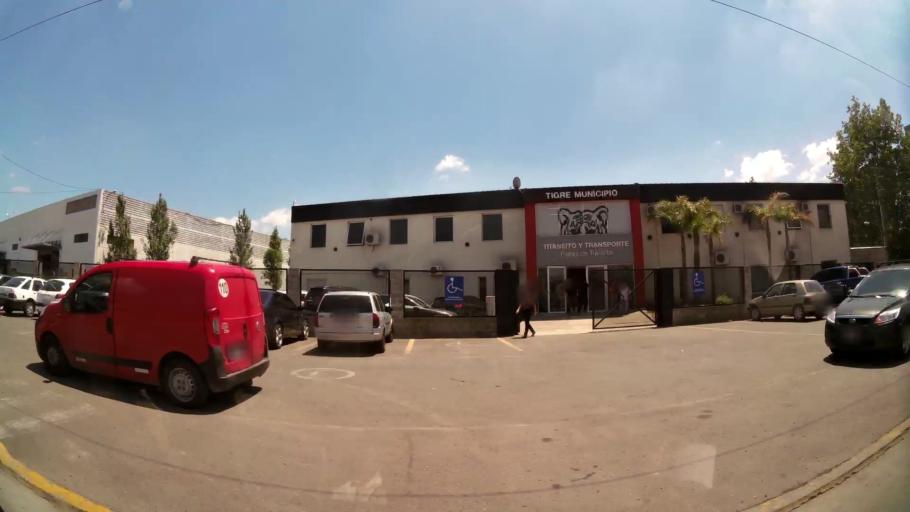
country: AR
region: Buenos Aires
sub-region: Partido de Tigre
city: Tigre
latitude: -34.4422
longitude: -58.5883
